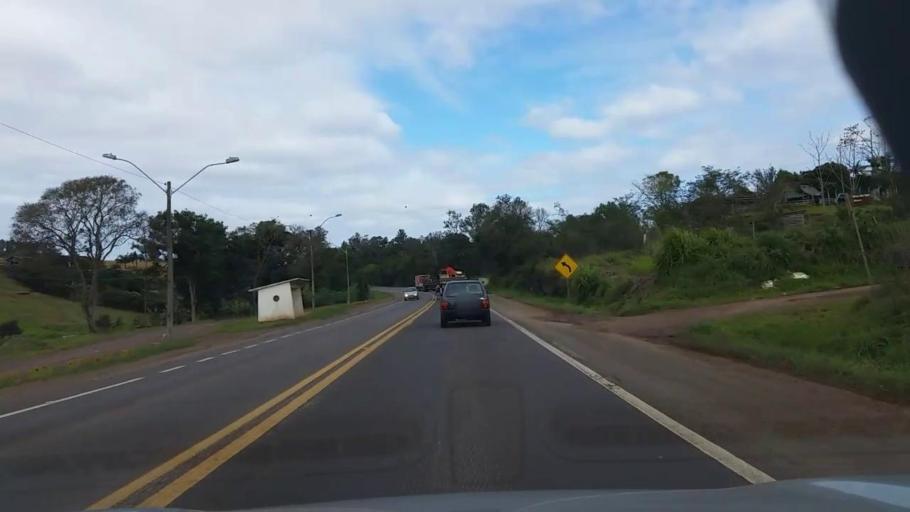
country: BR
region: Rio Grande do Sul
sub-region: Arroio Do Meio
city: Arroio do Meio
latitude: -29.4151
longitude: -52.0252
